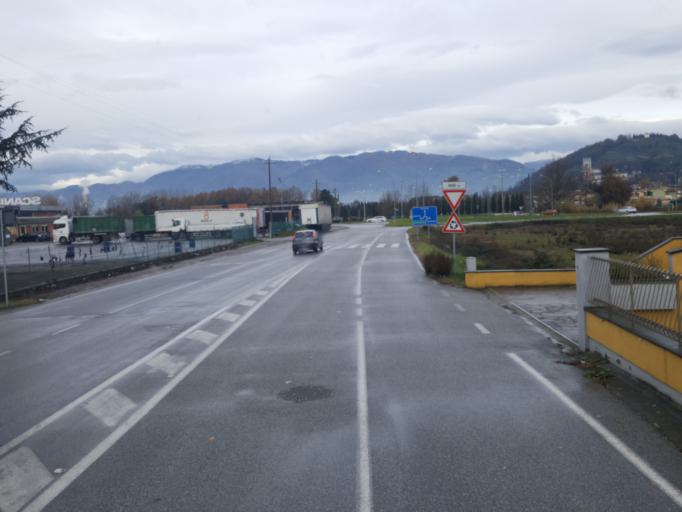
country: IT
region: Tuscany
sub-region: Provincia di Lucca
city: Porcari
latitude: 43.8330
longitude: 10.6155
